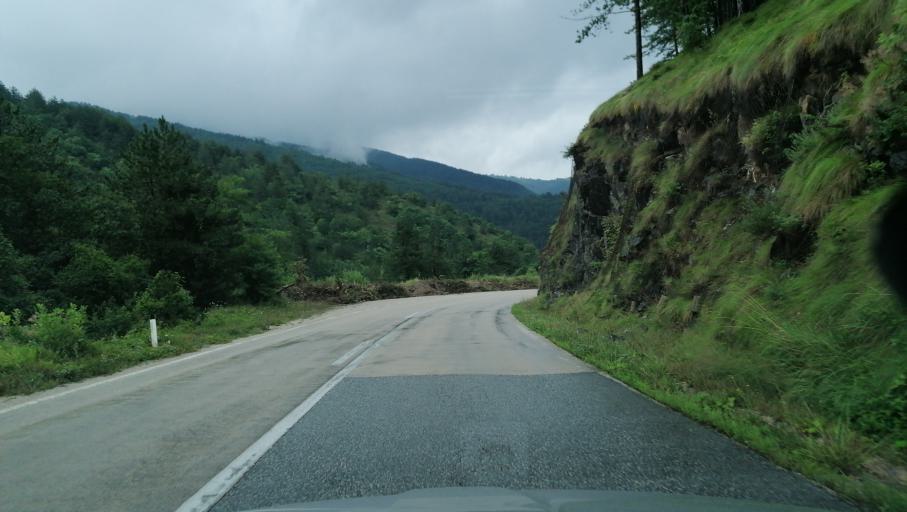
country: RS
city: Durici
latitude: 43.8175
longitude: 19.5108
